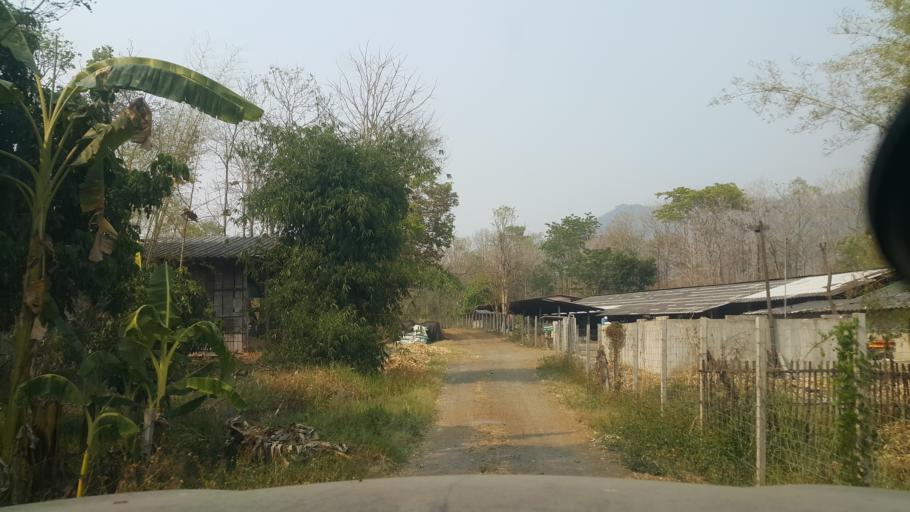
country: TH
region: Chiang Mai
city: Mae On
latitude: 18.7736
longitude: 99.2701
